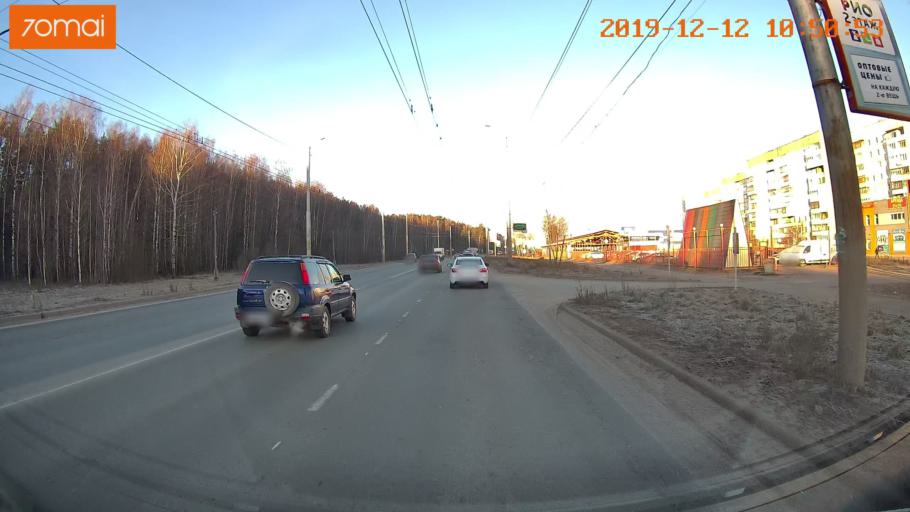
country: RU
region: Ivanovo
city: Kokhma
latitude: 56.9501
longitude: 41.0486
